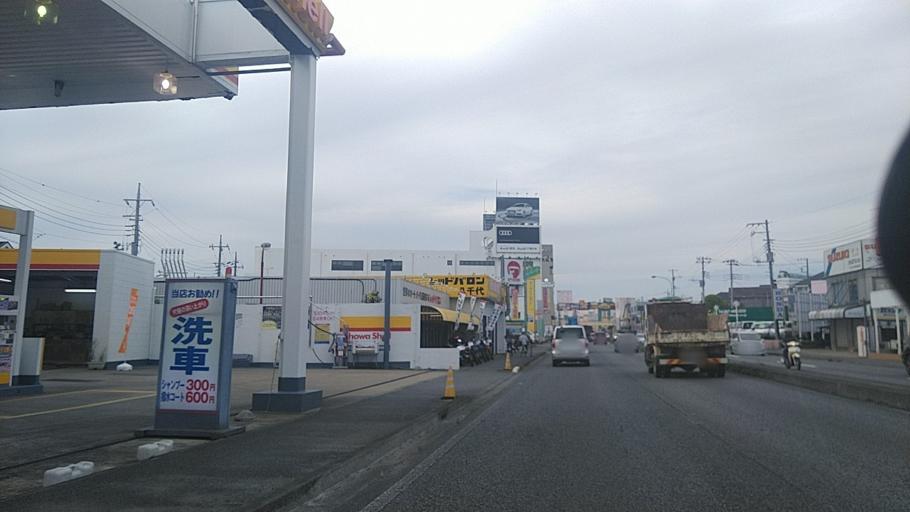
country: JP
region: Chiba
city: Yotsukaido
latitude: 35.7089
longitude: 140.1195
